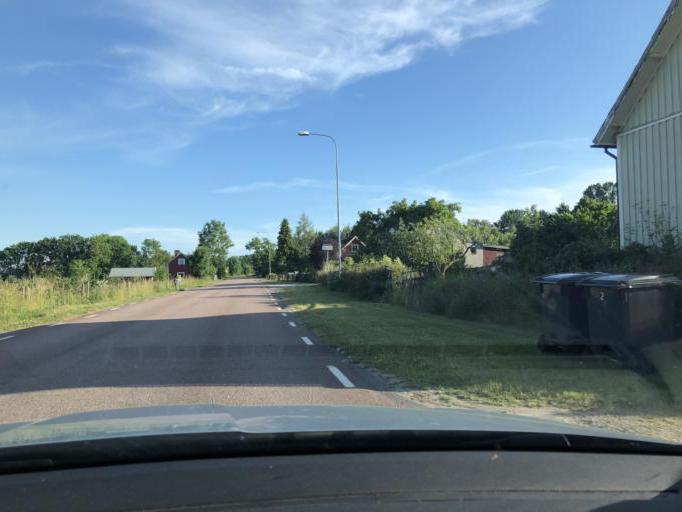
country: SE
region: Blekinge
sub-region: Solvesborgs Kommun
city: Soelvesborg
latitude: 56.1516
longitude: 14.6031
